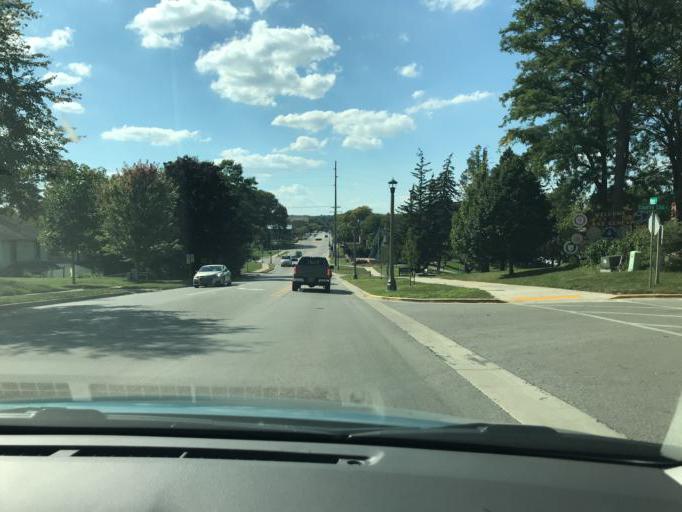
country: US
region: Wisconsin
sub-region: Walworth County
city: Lake Geneva
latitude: 42.5917
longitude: -88.4283
